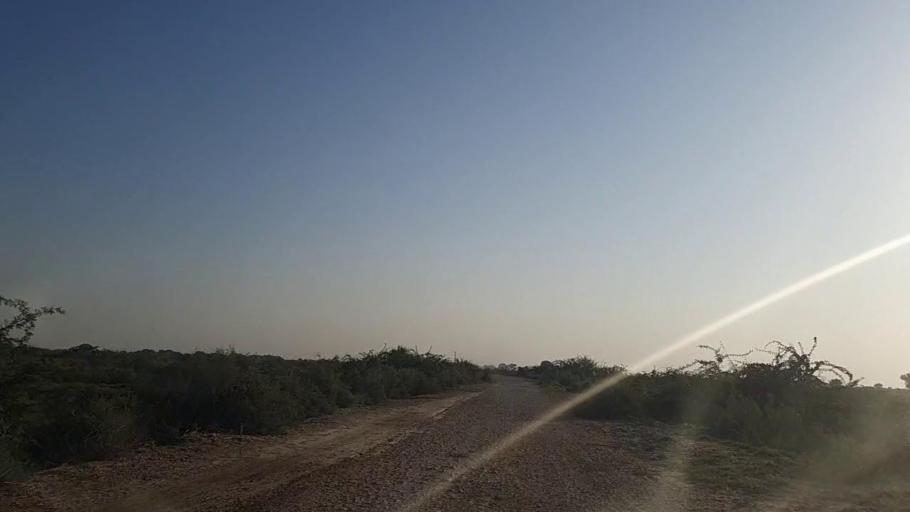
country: PK
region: Sindh
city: Jati
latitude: 24.4384
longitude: 68.1930
